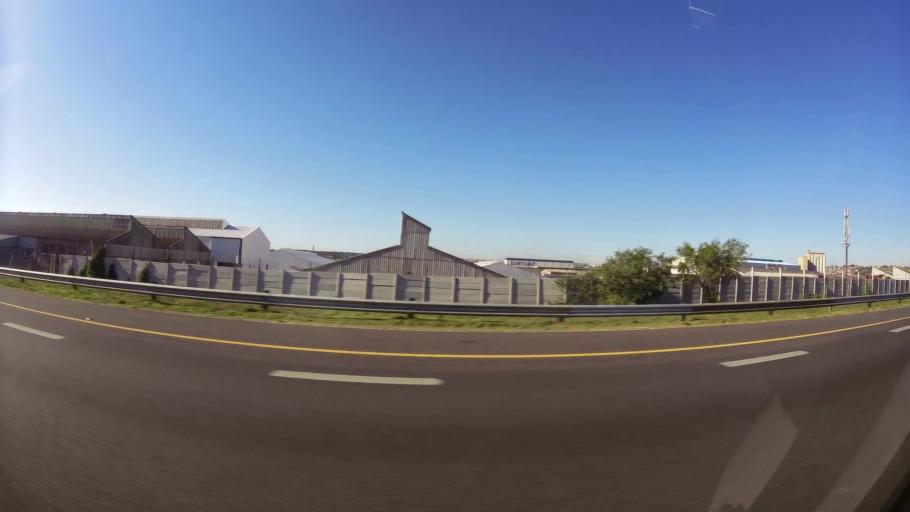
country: ZA
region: Eastern Cape
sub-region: Nelson Mandela Bay Metropolitan Municipality
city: Port Elizabeth
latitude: -33.9164
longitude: 25.5758
